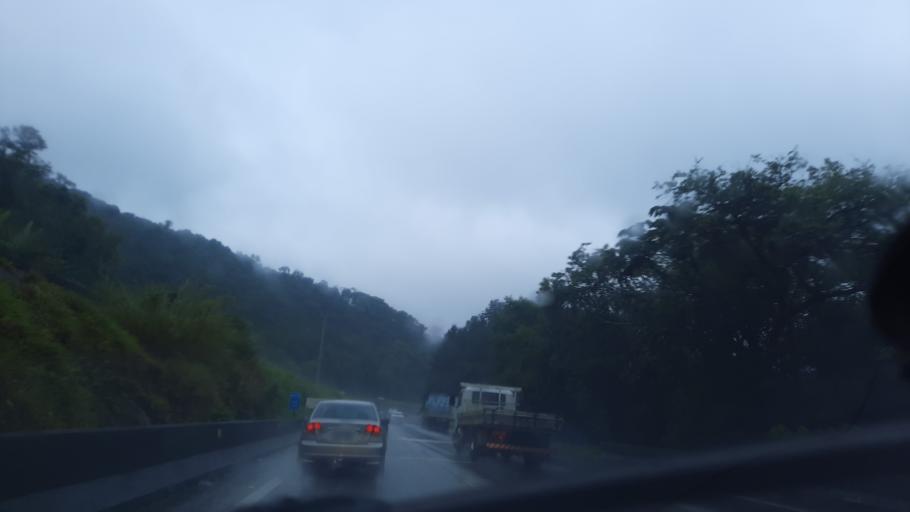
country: BR
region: Sao Paulo
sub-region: Mairipora
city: Mairipora
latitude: -23.3928
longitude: -46.5715
